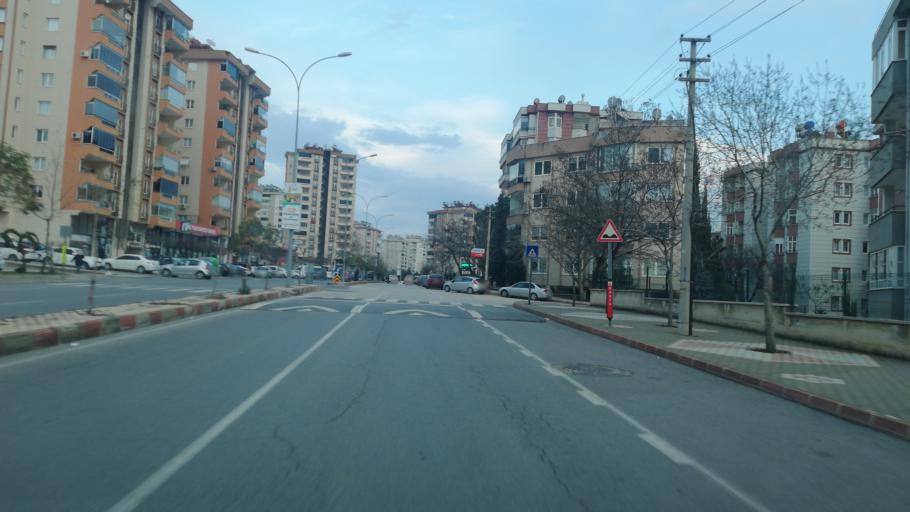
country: TR
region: Kahramanmaras
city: Kahramanmaras
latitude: 37.5867
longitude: 36.8851
